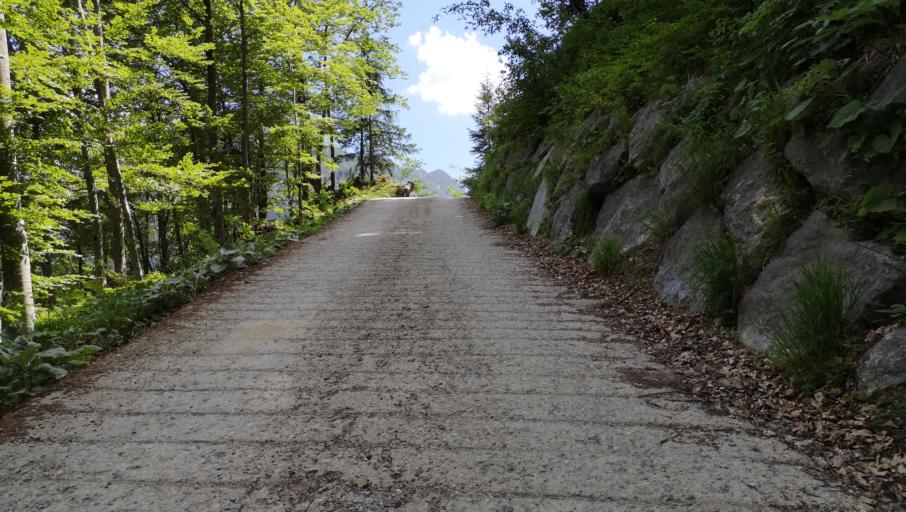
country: IT
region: Friuli Venezia Giulia
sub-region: Provincia di Udine
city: Pontebba
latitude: 46.5097
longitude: 13.2494
